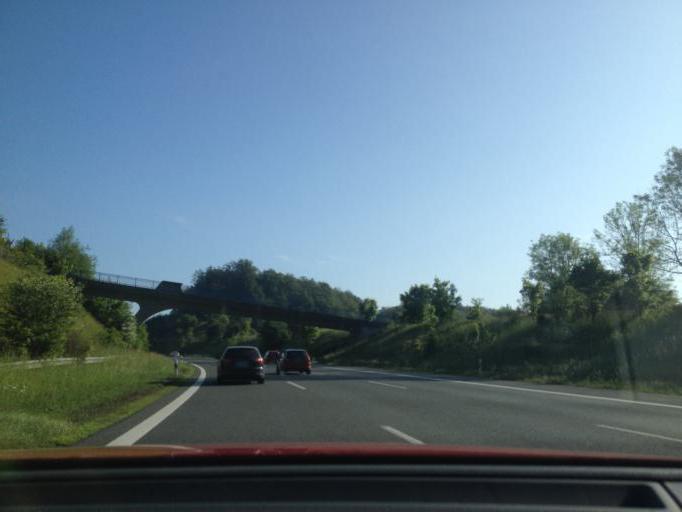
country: DE
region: Bavaria
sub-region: Regierungsbezirk Mittelfranken
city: Simmelsdorf
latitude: 49.5939
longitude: 11.3616
